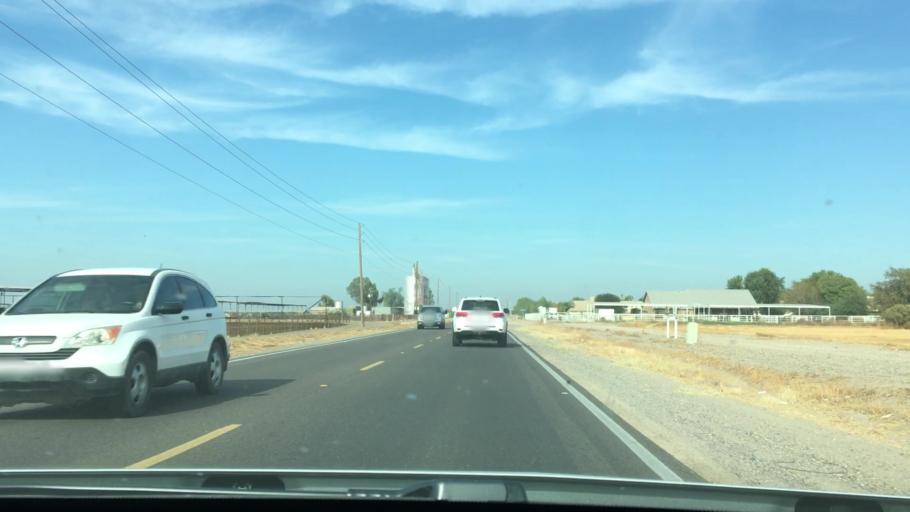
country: US
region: Arizona
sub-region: Maricopa County
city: Chandler
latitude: 33.2364
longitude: -111.7554
